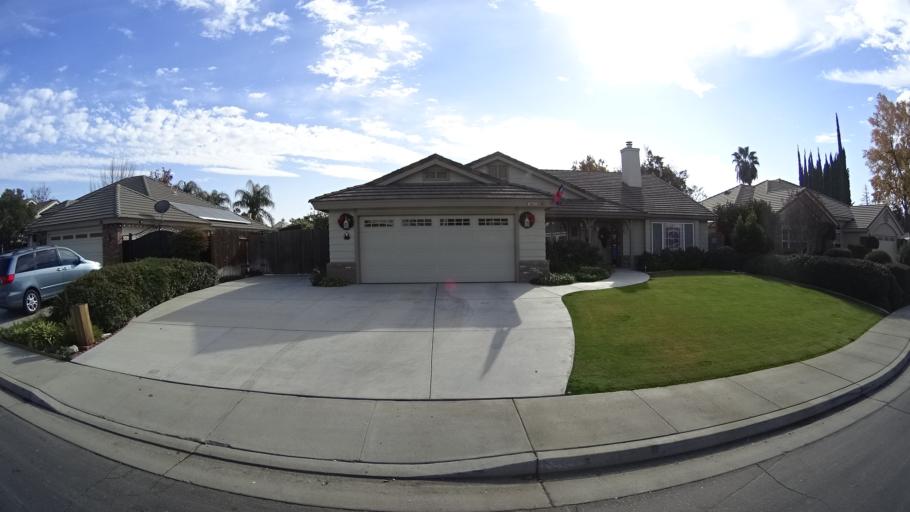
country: US
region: California
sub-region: Kern County
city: Greenacres
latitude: 35.4003
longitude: -119.1210
